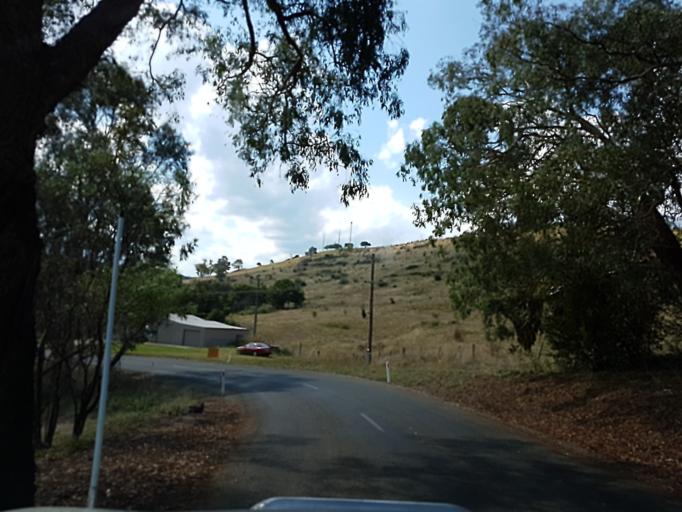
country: AU
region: Victoria
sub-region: East Gippsland
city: Lakes Entrance
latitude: -37.4982
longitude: 148.1832
